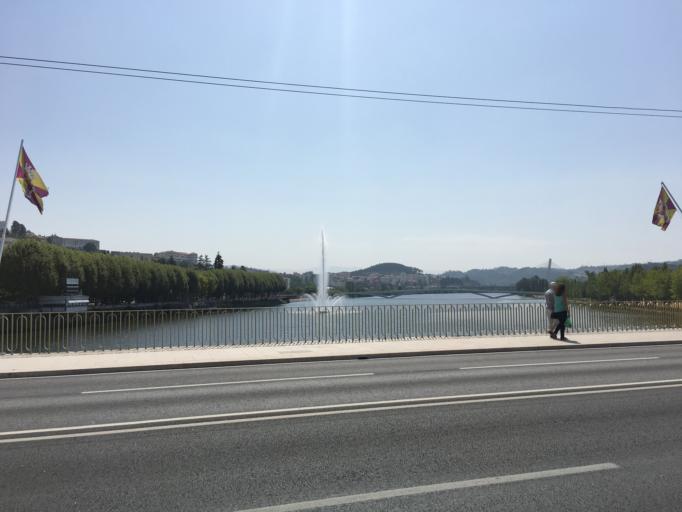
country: PT
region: Coimbra
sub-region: Coimbra
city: Coimbra
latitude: 40.2064
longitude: -8.4303
